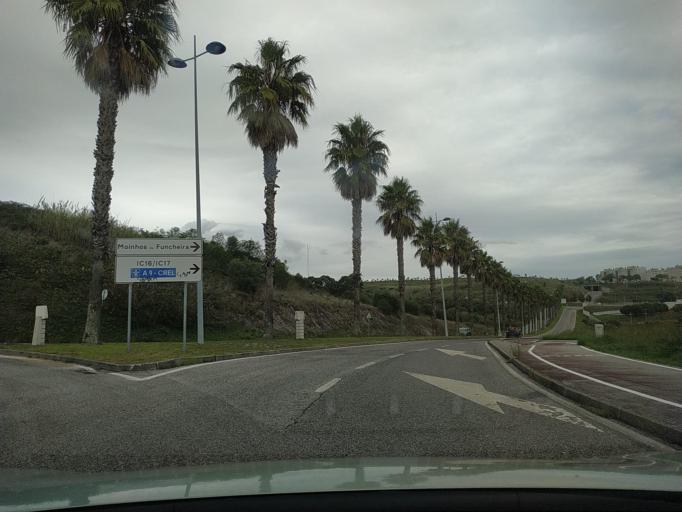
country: PT
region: Lisbon
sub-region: Amadora
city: Amadora
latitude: 38.7701
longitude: -9.2352
